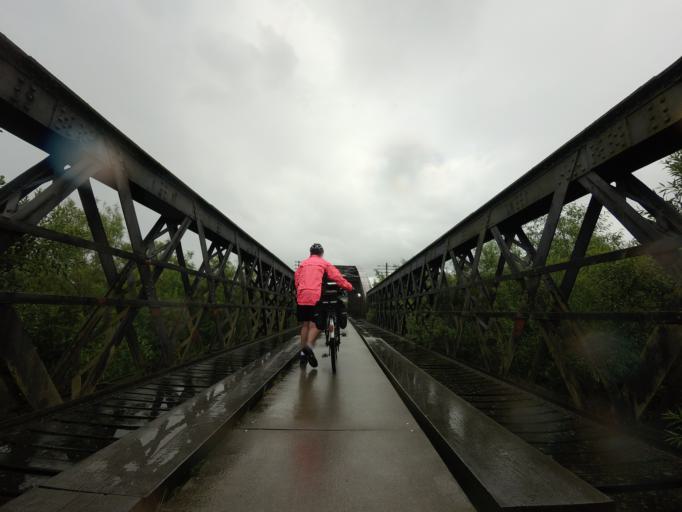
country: GB
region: Scotland
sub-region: Moray
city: Fochabers
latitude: 57.6630
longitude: -3.0977
